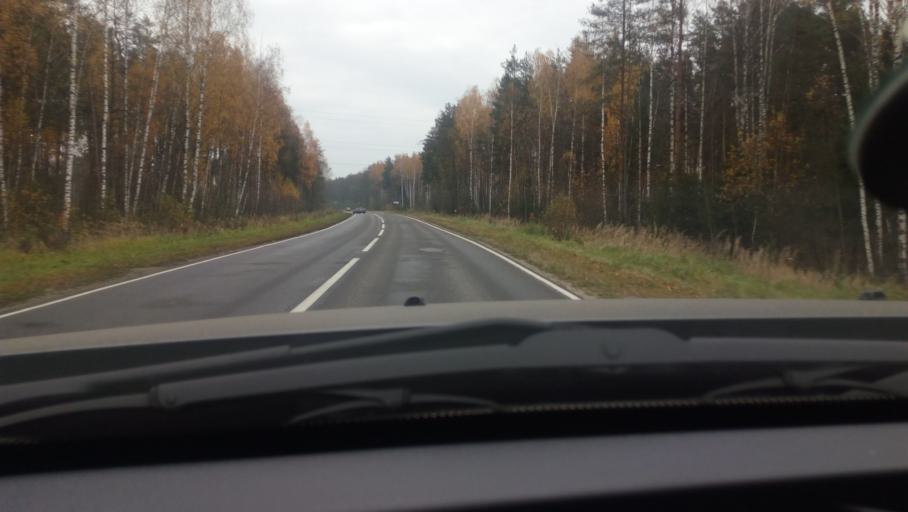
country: RU
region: Moskovskaya
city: Likino-Dulevo
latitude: 55.6972
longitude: 38.9069
